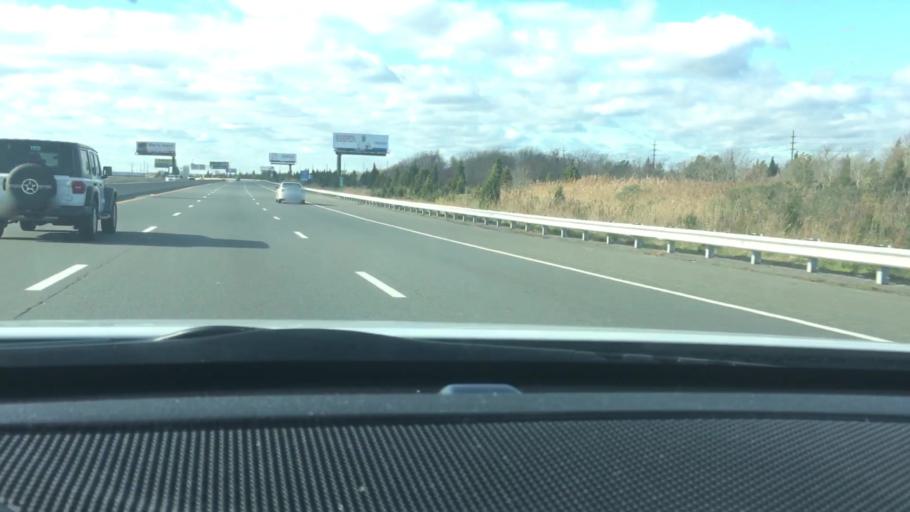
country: US
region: New Jersey
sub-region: Atlantic County
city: Atlantic City
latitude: 39.3653
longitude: -74.4507
